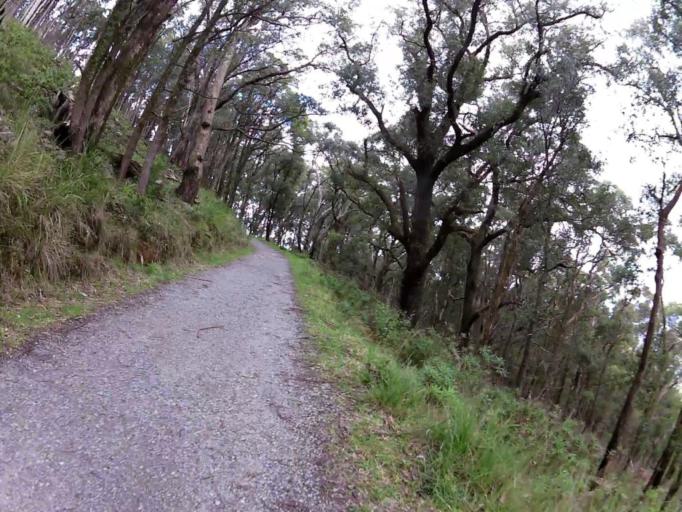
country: AU
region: Victoria
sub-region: Yarra Ranges
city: Montrose
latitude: -37.8359
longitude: 145.3465
